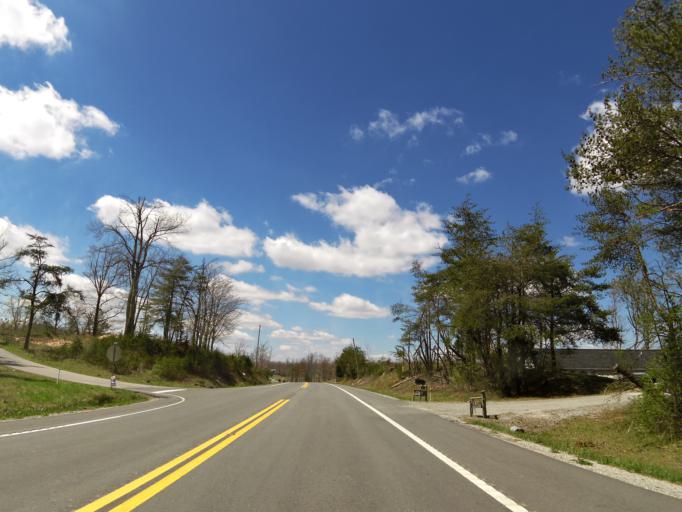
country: US
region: Tennessee
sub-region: Putnam County
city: Monterey
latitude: 35.9664
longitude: -85.2552
